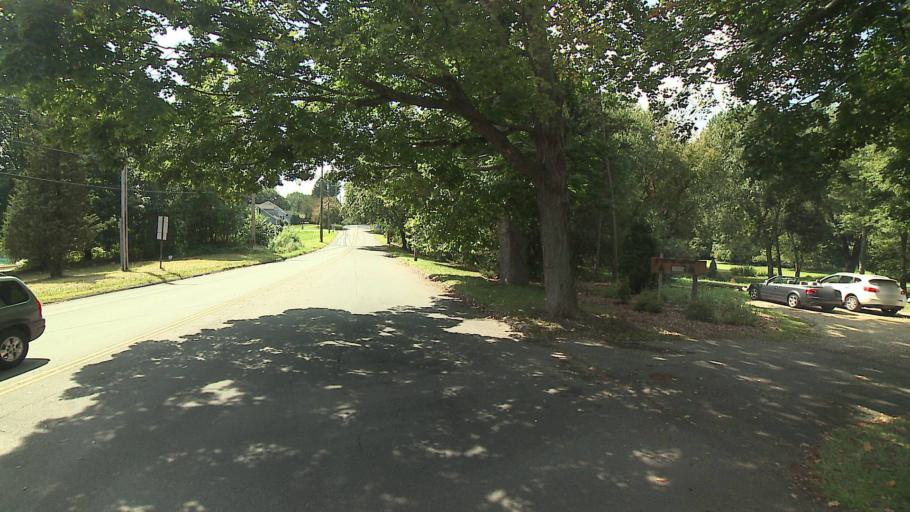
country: US
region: Connecticut
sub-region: Fairfield County
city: Trumbull
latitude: 41.2568
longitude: -73.1466
